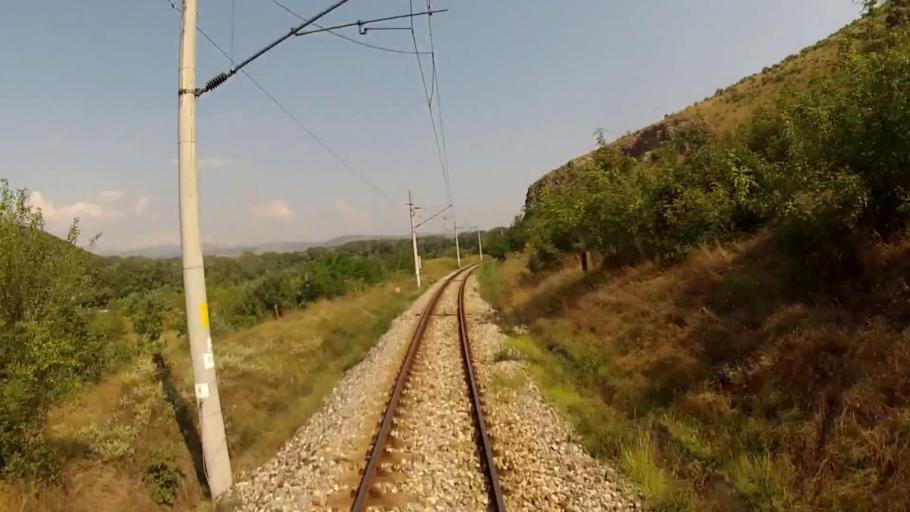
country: BG
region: Blagoevgrad
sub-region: Obshtina Petrich
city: Petrich
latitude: 41.4714
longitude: 23.2736
